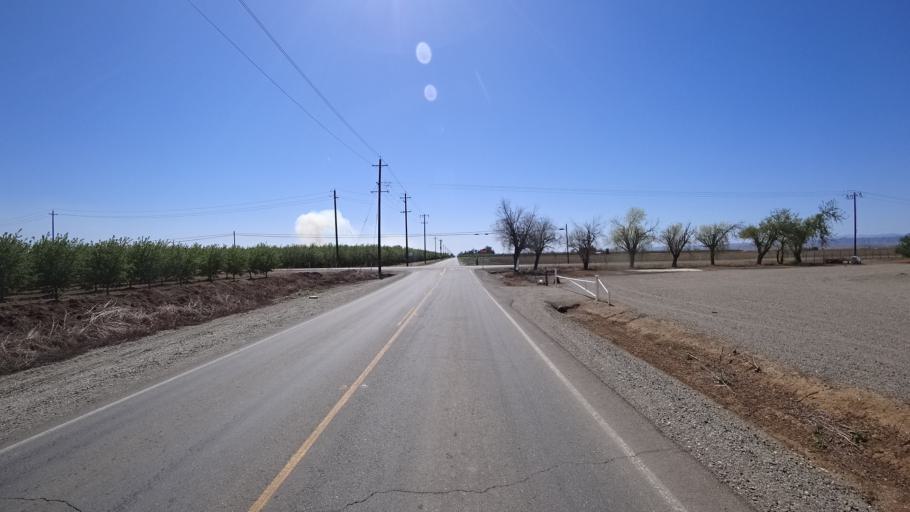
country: US
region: California
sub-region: Glenn County
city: Willows
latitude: 39.5248
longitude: -122.2493
